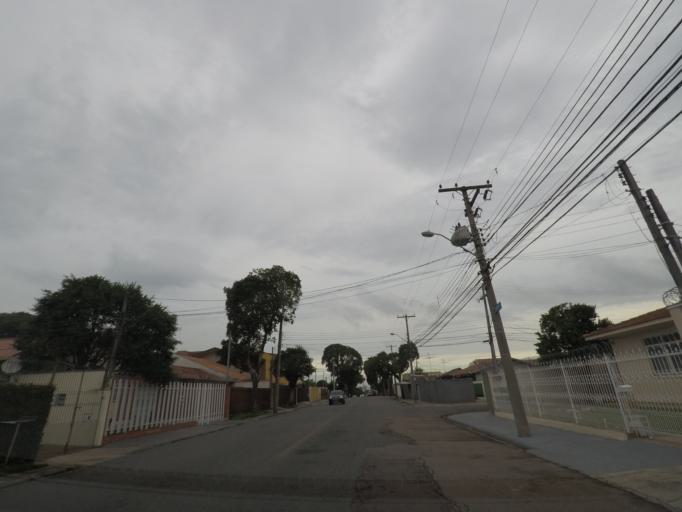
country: BR
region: Parana
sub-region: Curitiba
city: Curitiba
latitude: -25.4783
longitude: -49.3048
